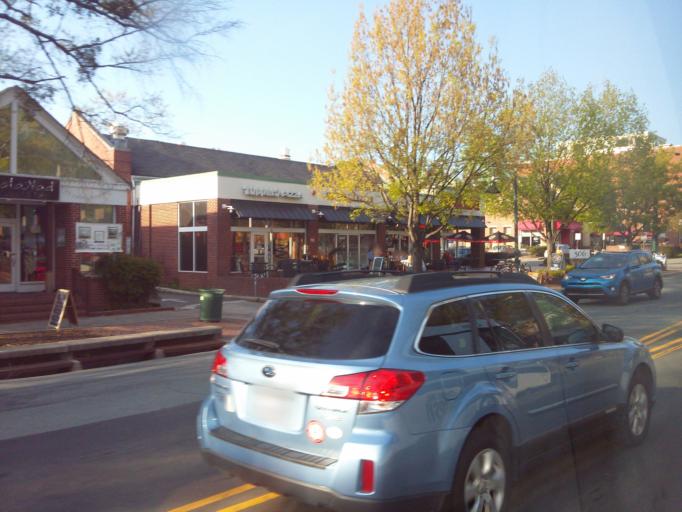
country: US
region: North Carolina
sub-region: Orange County
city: Chapel Hill
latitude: 35.9115
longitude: -79.0601
